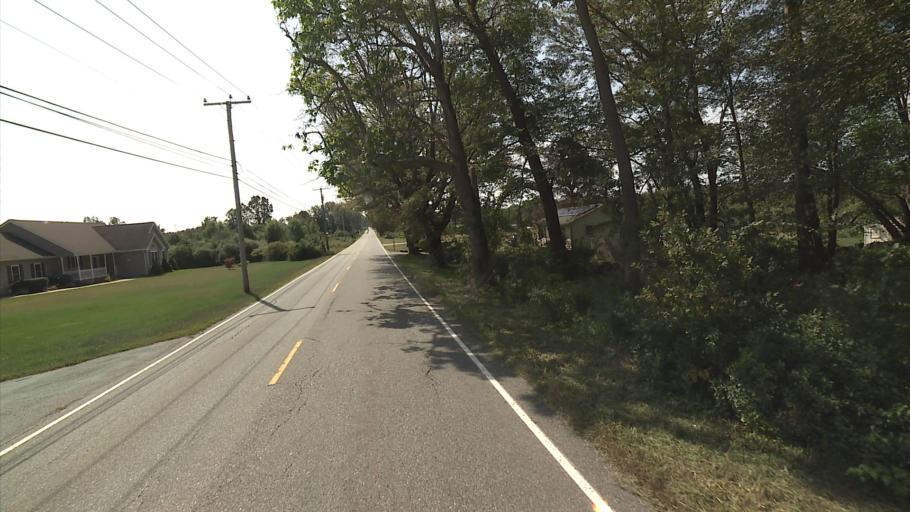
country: US
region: Connecticut
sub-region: Windham County
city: East Brooklyn
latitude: 41.8379
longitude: -71.9588
